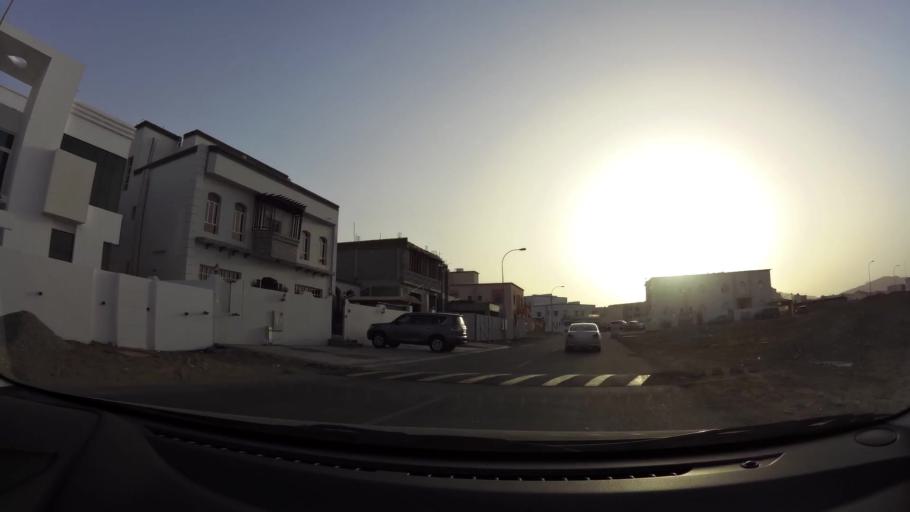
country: OM
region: Muhafazat Masqat
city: Bawshar
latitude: 23.4995
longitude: 58.3362
